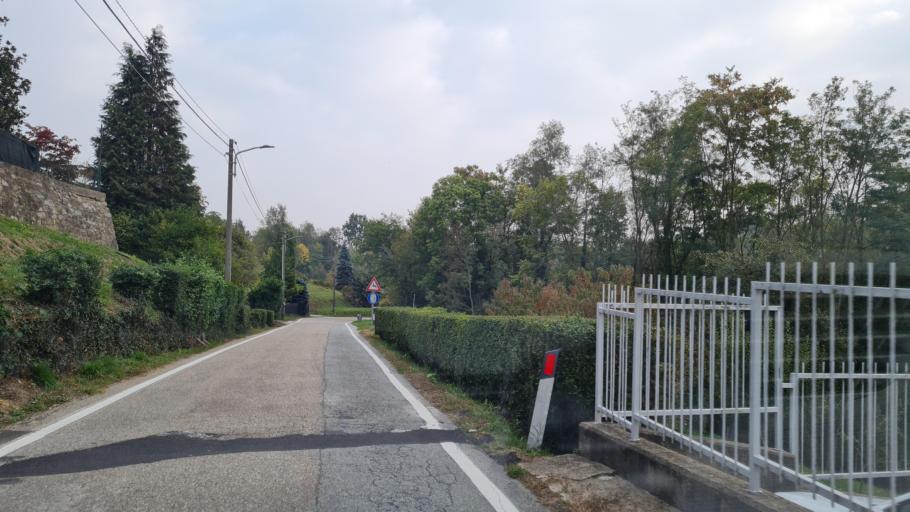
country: IT
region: Piedmont
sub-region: Provincia di Biella
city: Mezzana Mortigliengo
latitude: 45.6222
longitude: 8.1826
